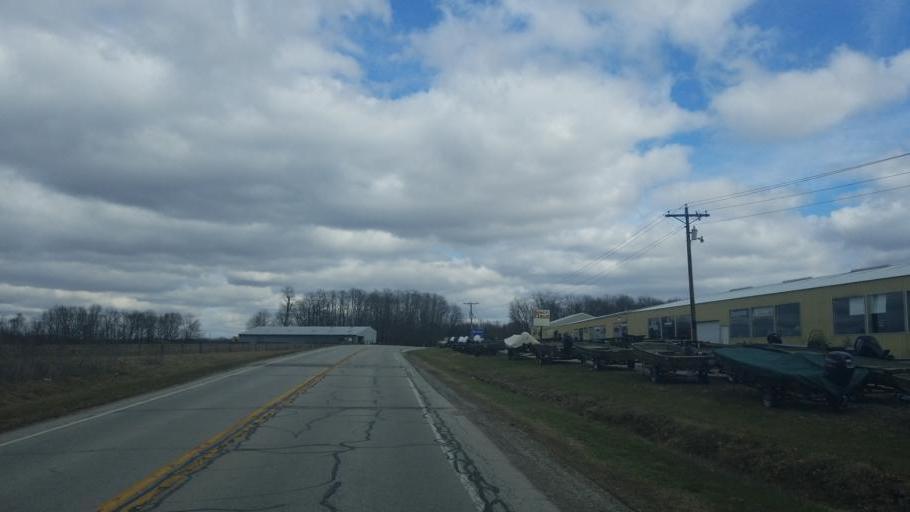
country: US
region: Indiana
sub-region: Parke County
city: Rockville
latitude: 39.7579
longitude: -87.0342
